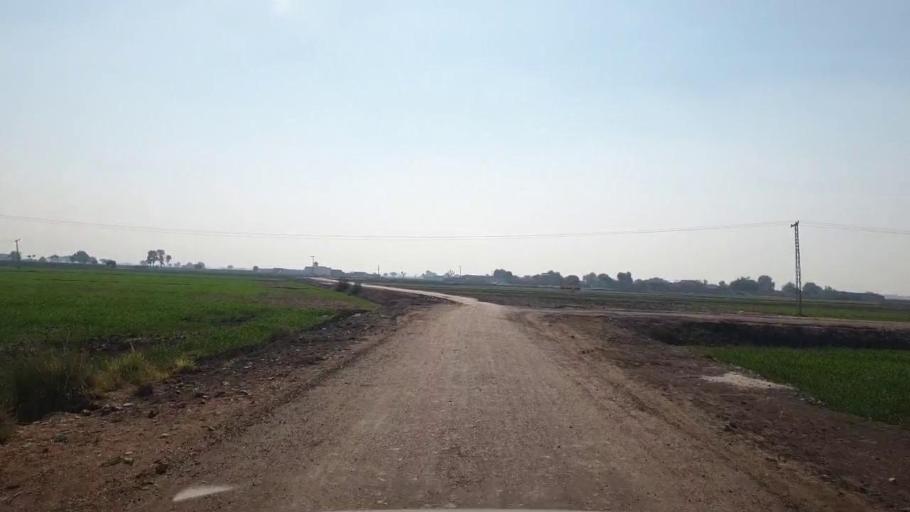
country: PK
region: Sindh
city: Bhan
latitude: 26.6499
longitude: 67.7017
